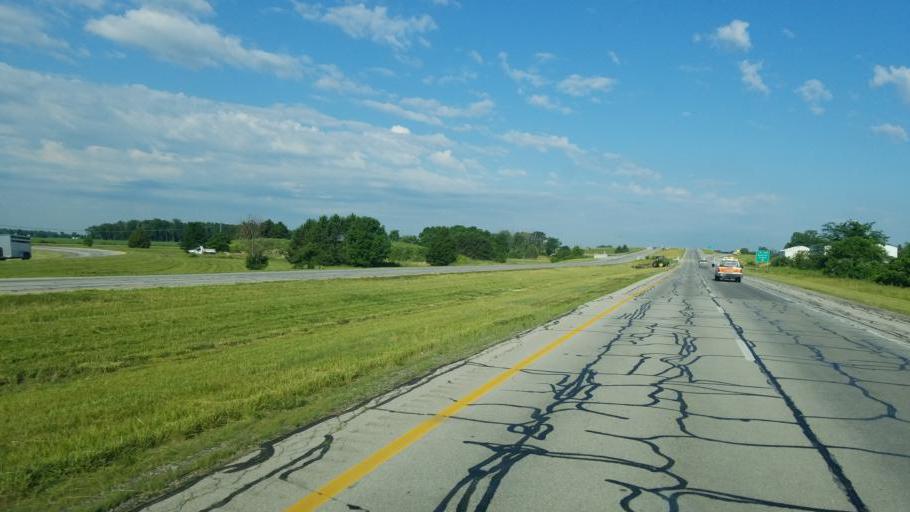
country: US
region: Ohio
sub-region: Crawford County
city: Bucyrus
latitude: 40.8271
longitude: -83.0338
